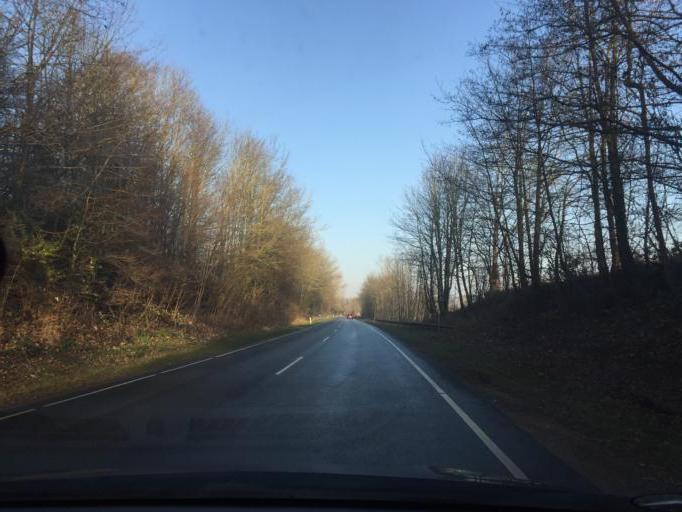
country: DK
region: South Denmark
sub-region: Faaborg-Midtfyn Kommune
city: Faaborg
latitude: 55.1623
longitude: 10.2748
